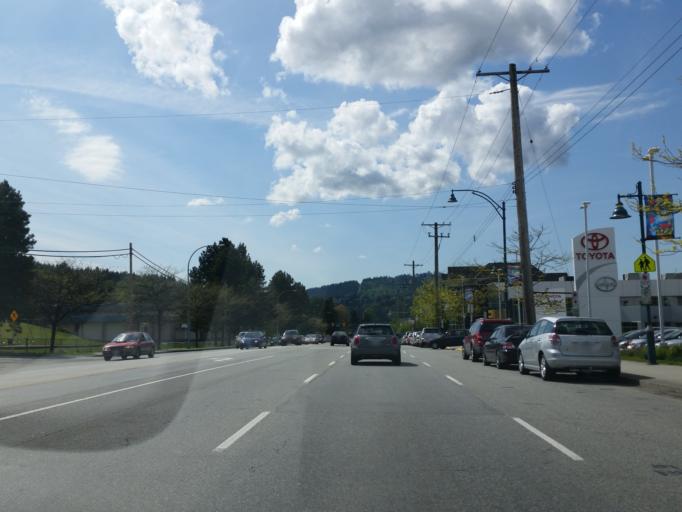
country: CA
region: British Columbia
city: Port Moody
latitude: 49.2767
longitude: -122.8364
